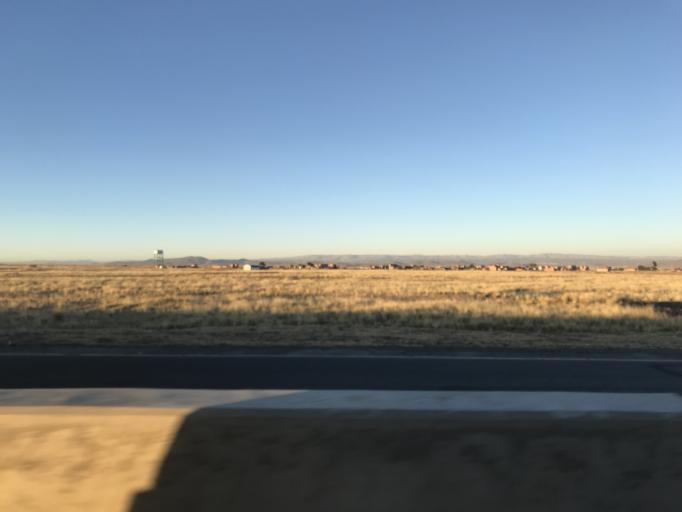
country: BO
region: La Paz
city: Batallas
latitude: -16.3102
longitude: -68.4589
